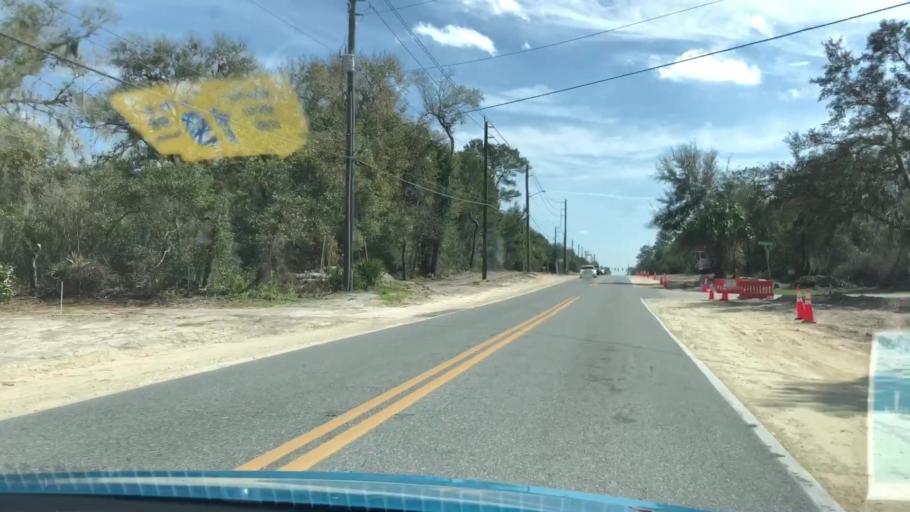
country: US
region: Florida
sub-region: Seminole County
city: Midway
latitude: 28.8578
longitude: -81.1912
